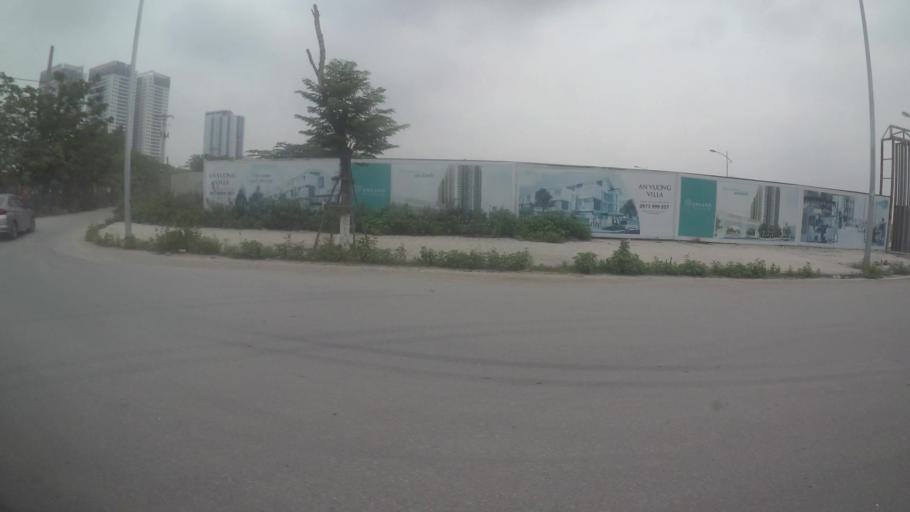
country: VN
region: Ha Noi
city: Ha Dong
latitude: 20.9881
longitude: 105.7534
